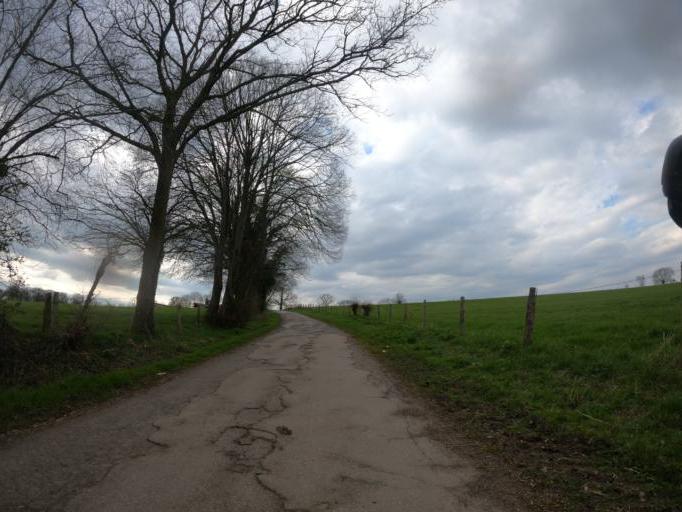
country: BE
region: Wallonia
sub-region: Province de Liege
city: Raeren
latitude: 50.7313
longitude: 6.1569
